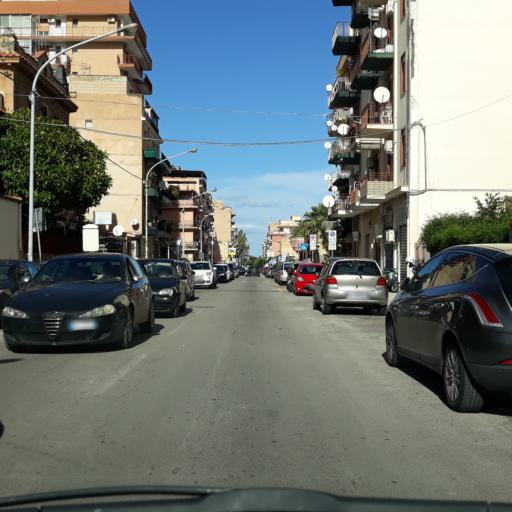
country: IT
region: Sicily
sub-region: Palermo
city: Palermo
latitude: 38.1494
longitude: 13.3708
